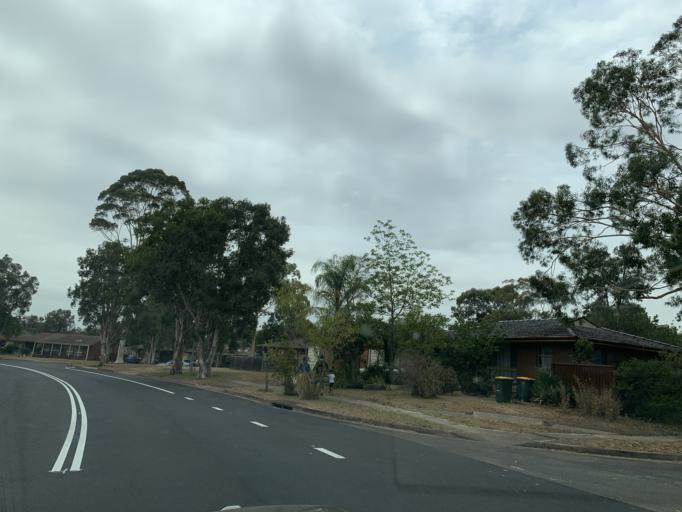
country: AU
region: New South Wales
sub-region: Blacktown
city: Doonside
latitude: -33.7524
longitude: 150.8750
